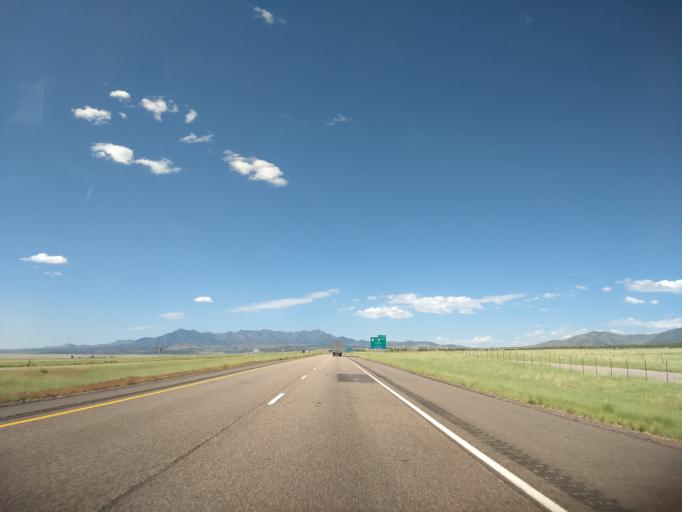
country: US
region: Utah
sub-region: Millard County
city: Fillmore
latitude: 39.0721
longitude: -112.2814
